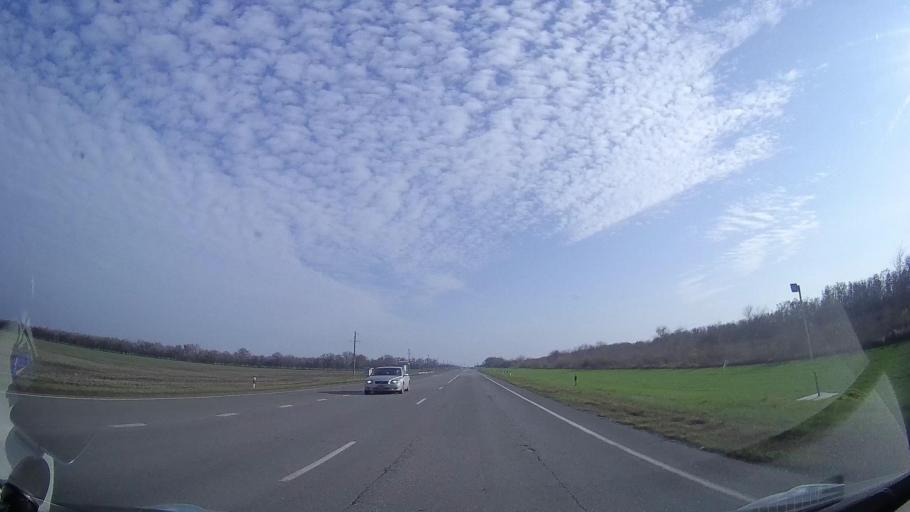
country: RU
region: Rostov
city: Gigant
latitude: 46.5264
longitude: 41.2255
